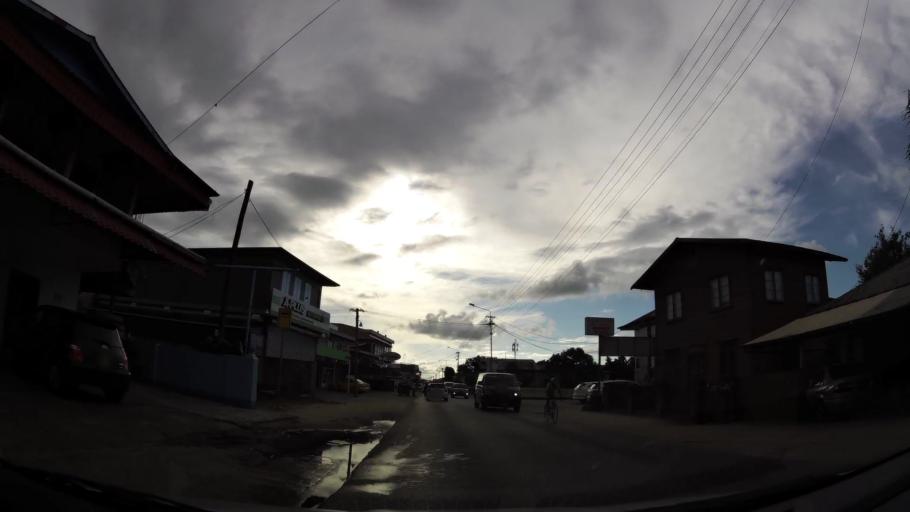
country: SR
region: Paramaribo
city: Paramaribo
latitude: 5.8379
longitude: -55.1772
